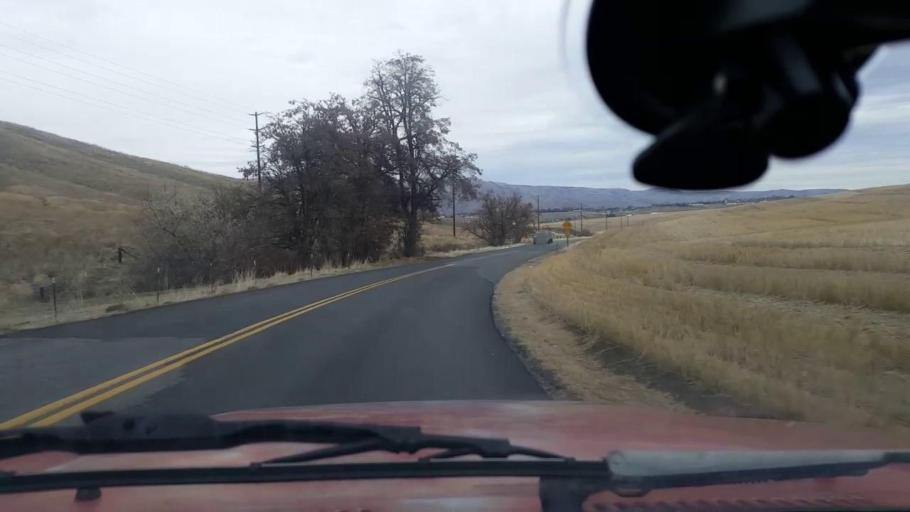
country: US
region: Washington
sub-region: Asotin County
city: Clarkston Heights-Vineland
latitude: 46.3863
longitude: -117.1132
